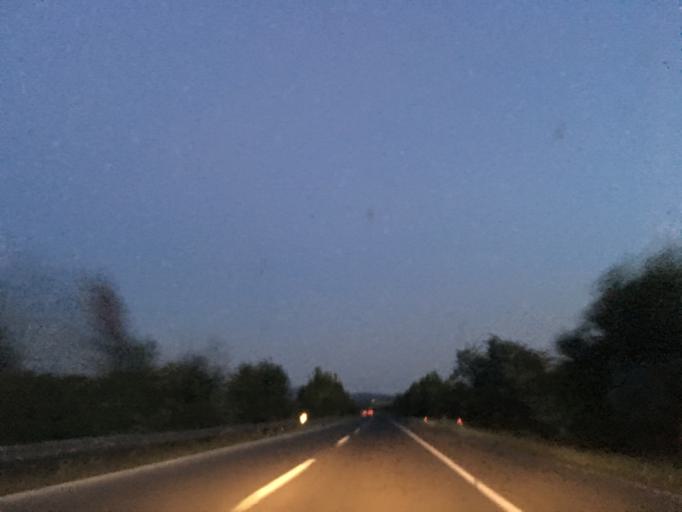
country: MK
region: Petrovec
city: Petrovec
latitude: 41.9166
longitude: 21.6402
